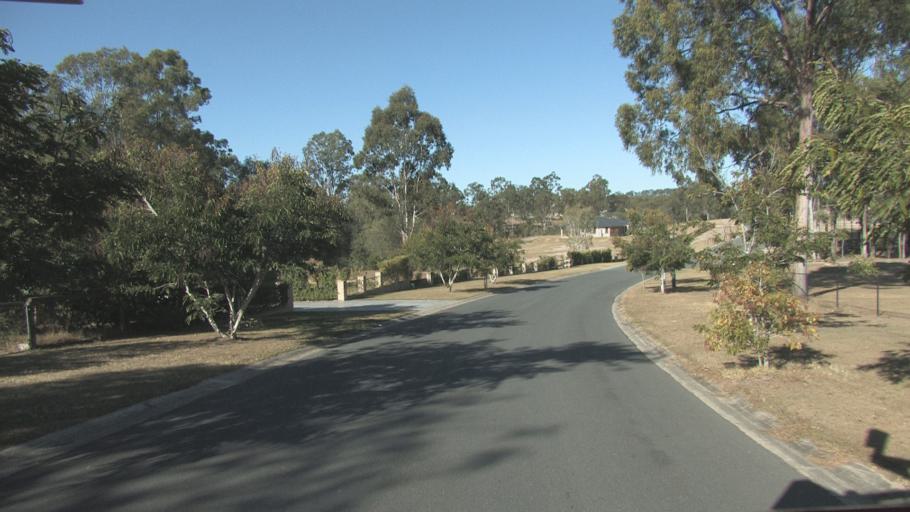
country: AU
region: Queensland
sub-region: Logan
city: Cedar Vale
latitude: -27.8684
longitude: 153.0393
